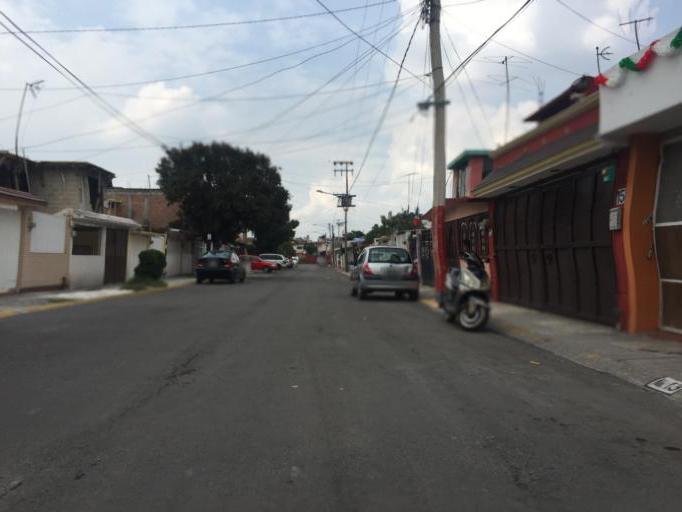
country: MX
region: Mexico
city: Cuautitlan Izcalli
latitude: 19.6567
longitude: -99.2168
